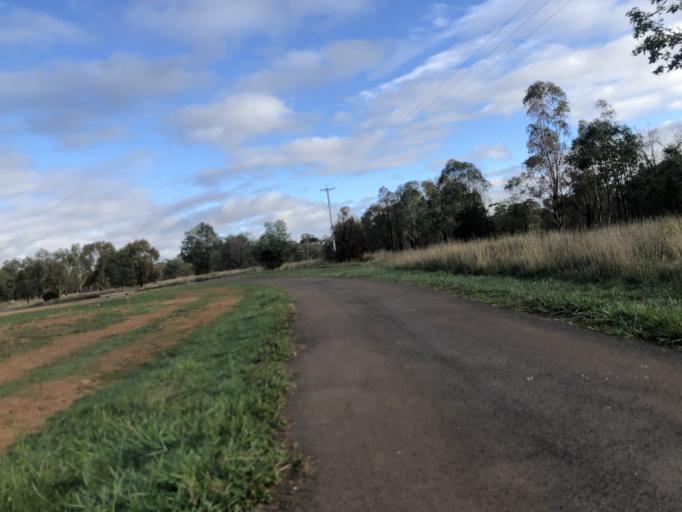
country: AU
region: New South Wales
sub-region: Orange Municipality
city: Orange
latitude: -33.3262
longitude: 149.0919
